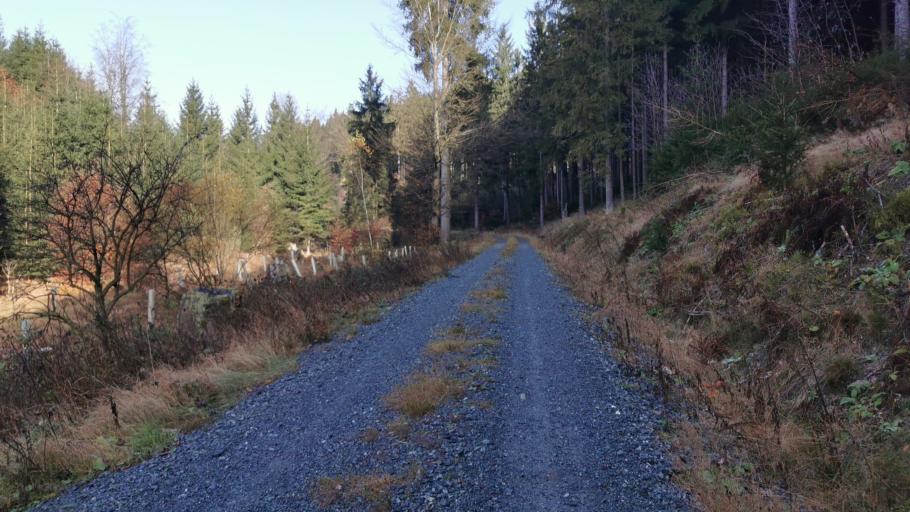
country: DE
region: Bavaria
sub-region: Upper Franconia
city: Tschirn
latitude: 50.4378
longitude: 11.4627
